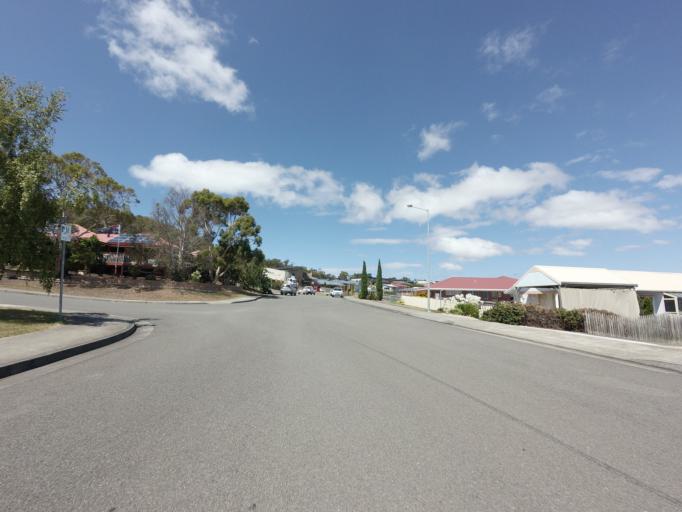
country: AU
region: Tasmania
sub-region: Clarence
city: Rokeby
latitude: -42.9010
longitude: 147.4585
